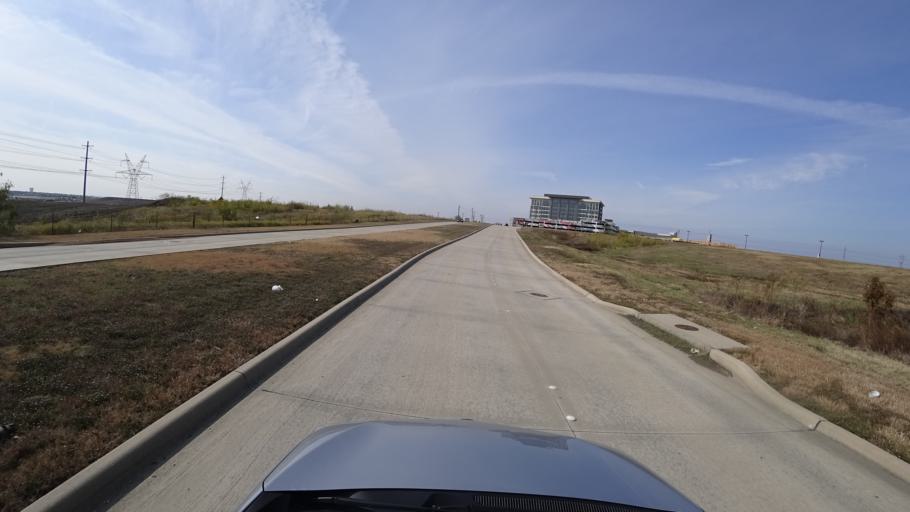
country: US
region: Texas
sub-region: Denton County
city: The Colony
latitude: 33.0605
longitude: -96.8896
